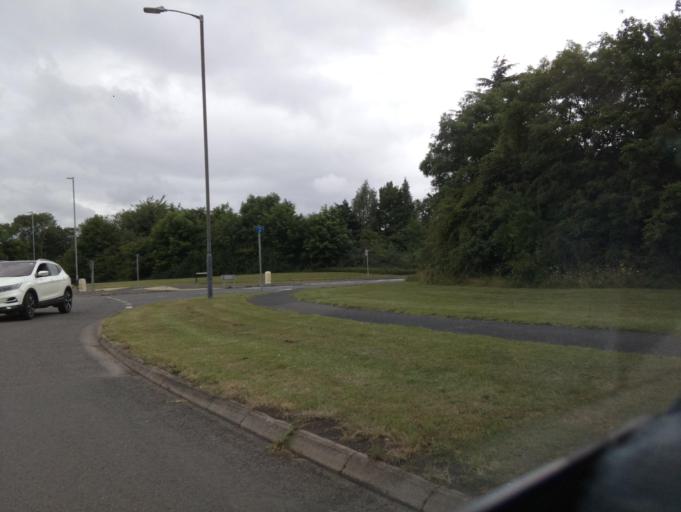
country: GB
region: England
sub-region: Worcestershire
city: Droitwich
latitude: 52.2524
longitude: -2.1619
